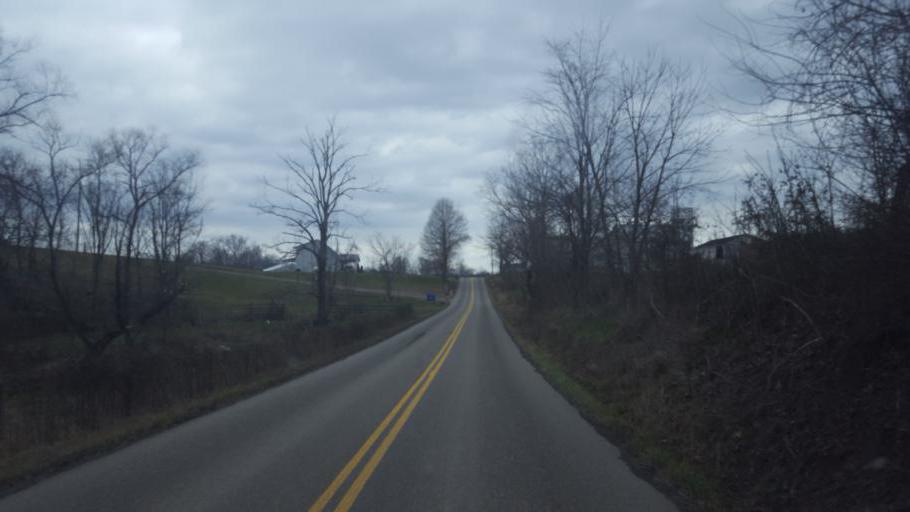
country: US
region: Ohio
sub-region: Gallia County
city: Gallipolis
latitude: 38.7276
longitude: -82.3654
